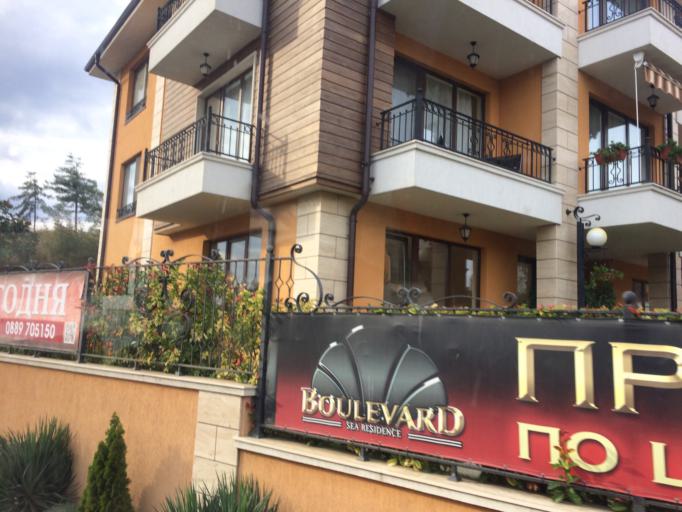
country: BG
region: Burgas
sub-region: Obshtina Nesebur
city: Sveti Vlas
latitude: 42.7103
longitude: 27.7277
